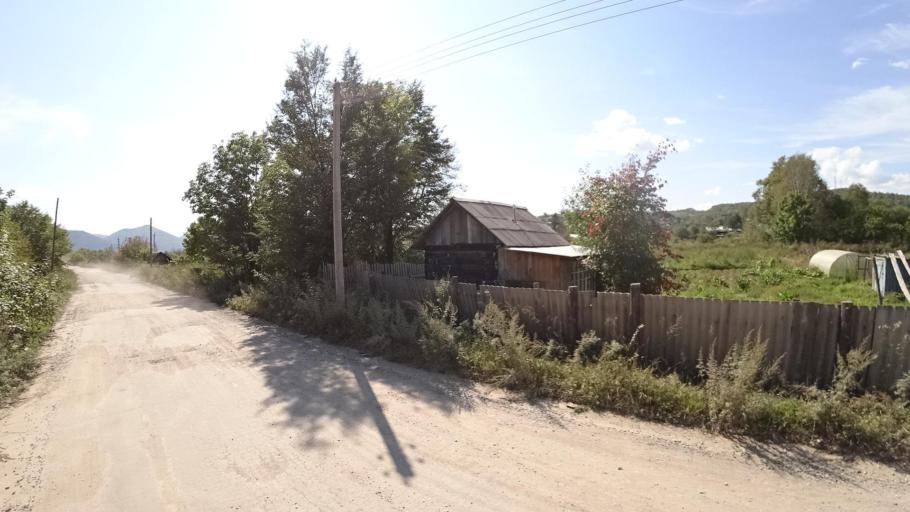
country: RU
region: Jewish Autonomous Oblast
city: Londoko
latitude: 49.0154
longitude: 131.8778
